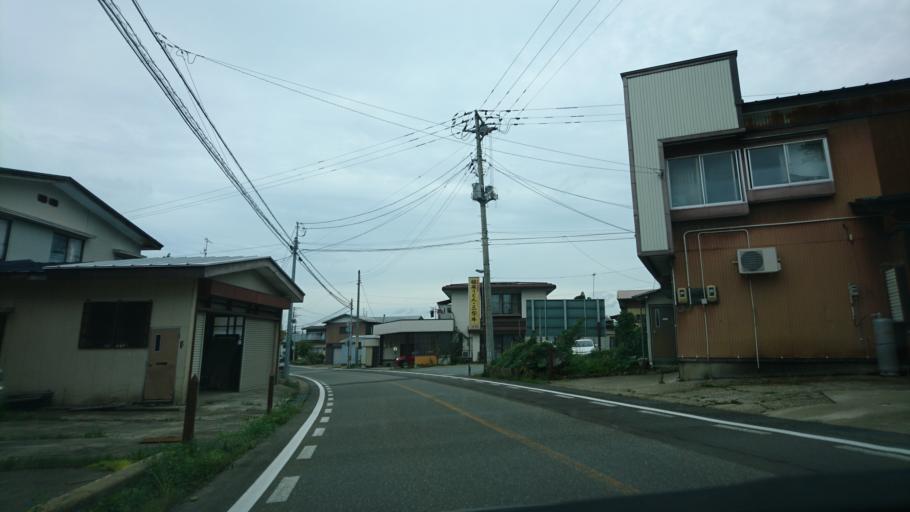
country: JP
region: Akita
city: Yuzawa
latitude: 39.1316
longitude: 140.5761
